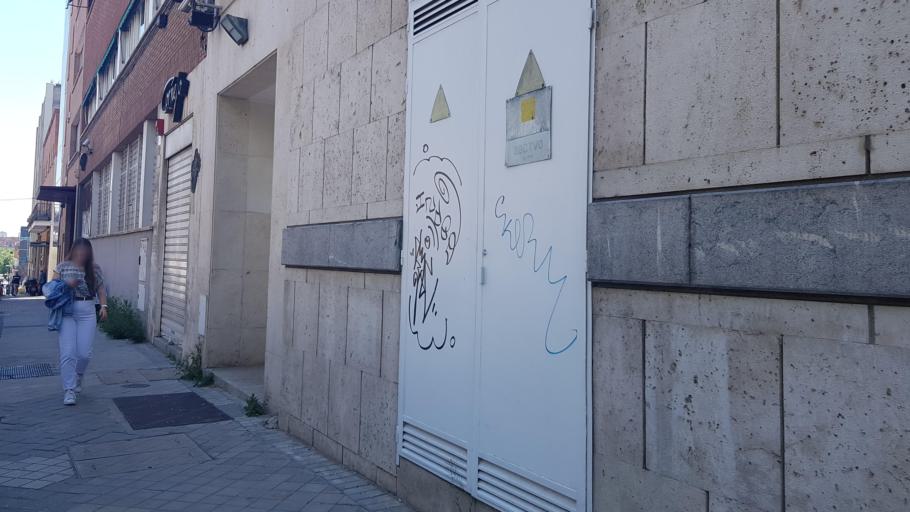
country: ES
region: Madrid
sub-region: Provincia de Madrid
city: San Blas
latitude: 40.4403
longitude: -3.6277
